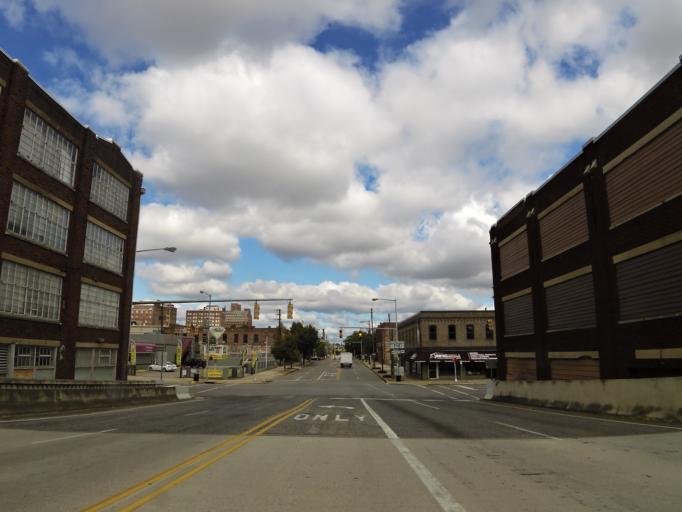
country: US
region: Alabama
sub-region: Jefferson County
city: Birmingham
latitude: 33.5167
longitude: -86.7998
